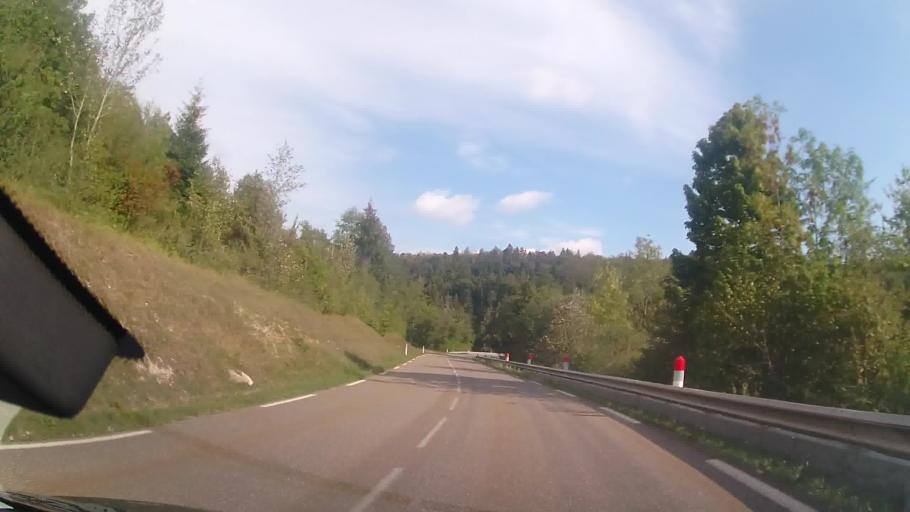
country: FR
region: Franche-Comte
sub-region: Departement du Jura
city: Clairvaux-les-Lacs
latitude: 46.5862
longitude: 5.8306
